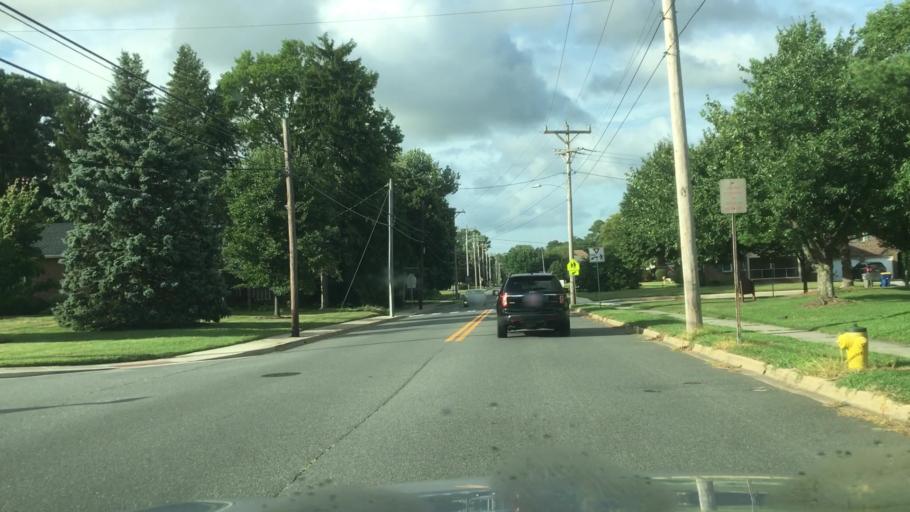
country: US
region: Delaware
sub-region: Sussex County
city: Milford
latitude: 38.9052
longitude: -75.4370
